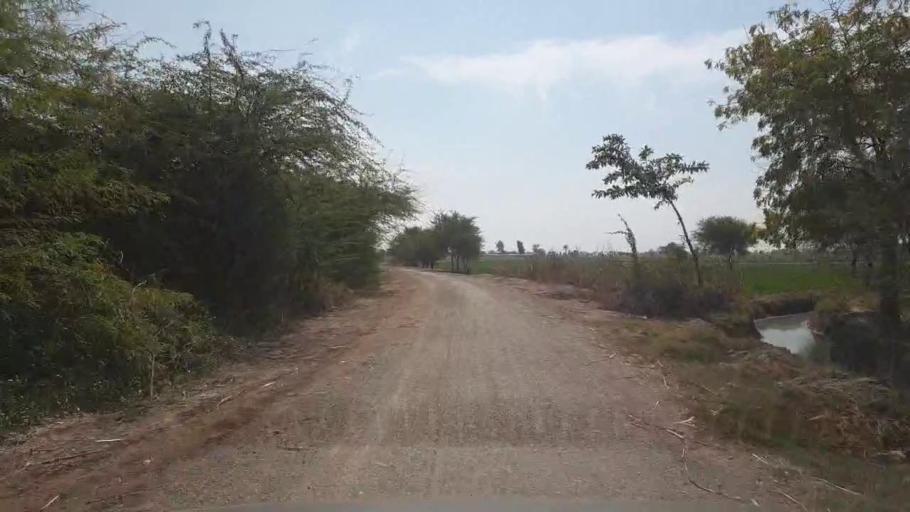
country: PK
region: Sindh
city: Mirwah Gorchani
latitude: 25.4404
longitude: 69.1927
